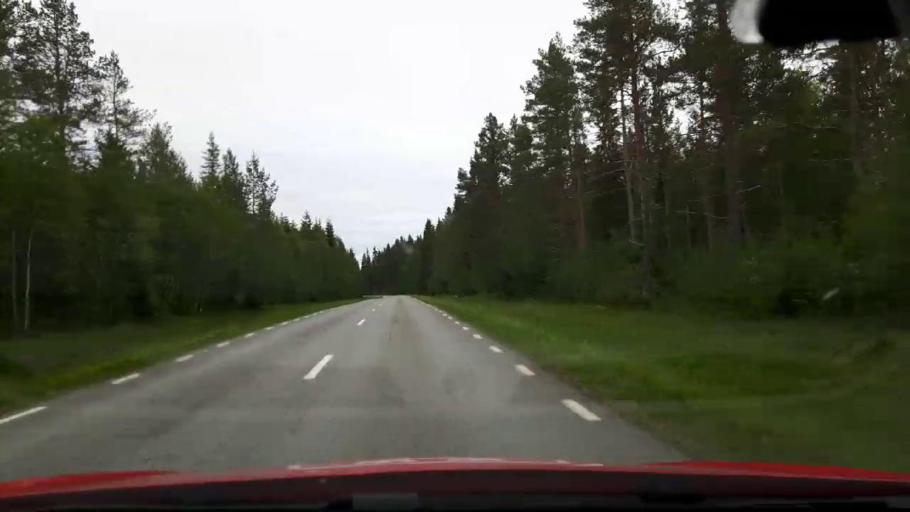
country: SE
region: Jaemtland
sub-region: Stroemsunds Kommun
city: Stroemsund
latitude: 63.4727
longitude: 15.4484
